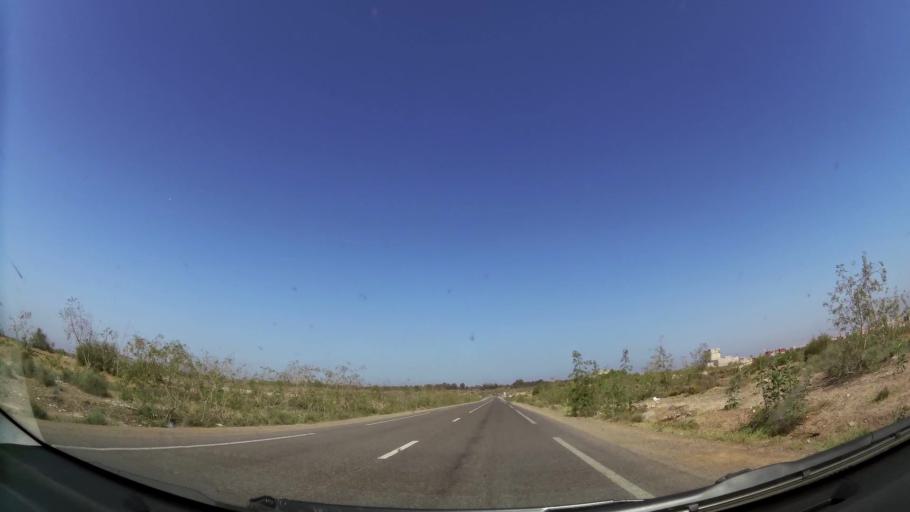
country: MA
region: Souss-Massa-Draa
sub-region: Inezgane-Ait Mellou
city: Inezgane
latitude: 30.3101
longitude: -9.5129
